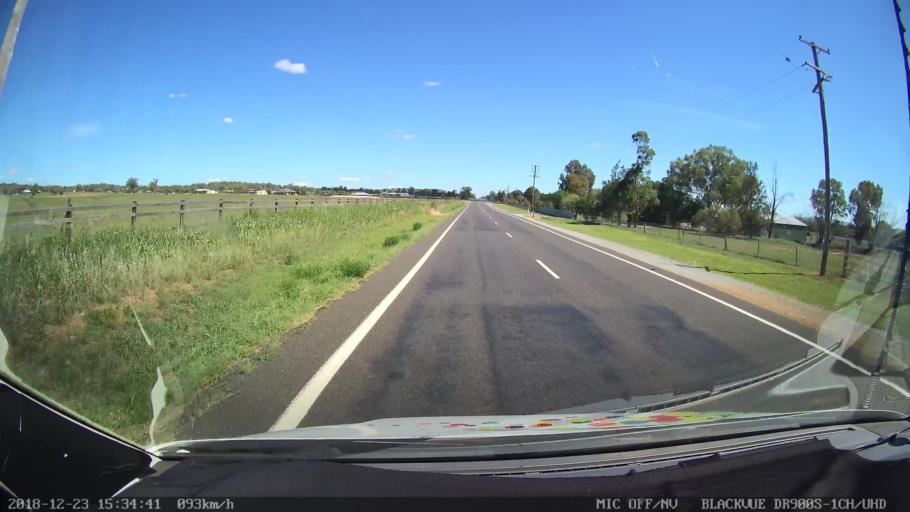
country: AU
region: New South Wales
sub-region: Tamworth Municipality
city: Tamworth
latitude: -31.0172
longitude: 150.8794
